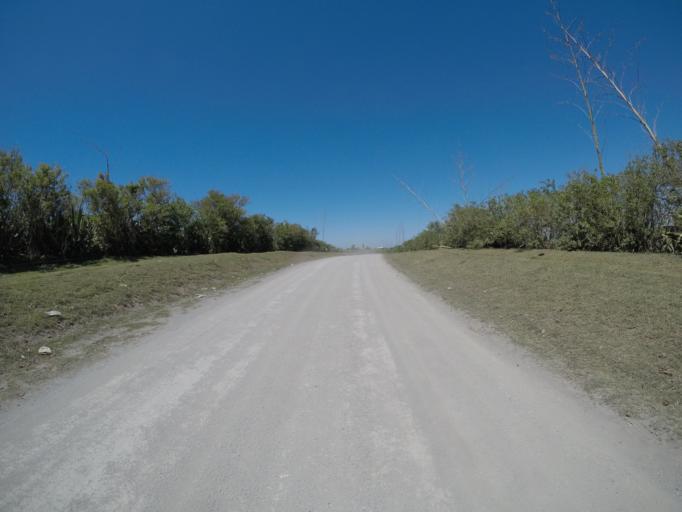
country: ZA
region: Eastern Cape
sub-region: OR Tambo District Municipality
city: Libode
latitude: -32.0050
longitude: 29.0731
